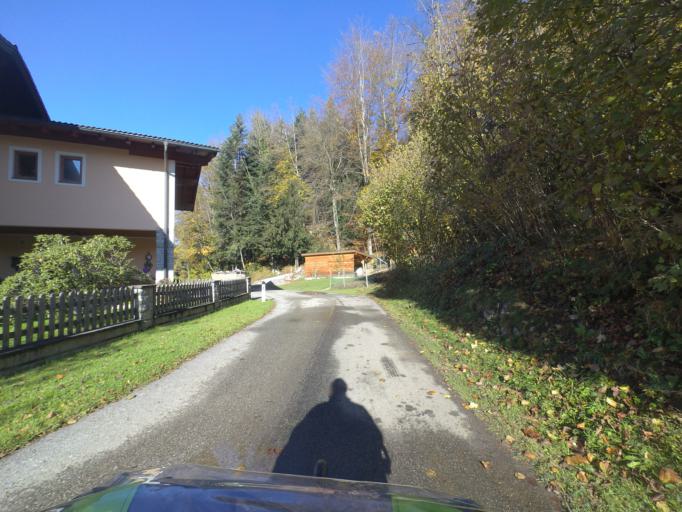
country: AT
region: Salzburg
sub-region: Politischer Bezirk Hallein
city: Adnet
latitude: 47.6710
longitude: 13.1586
